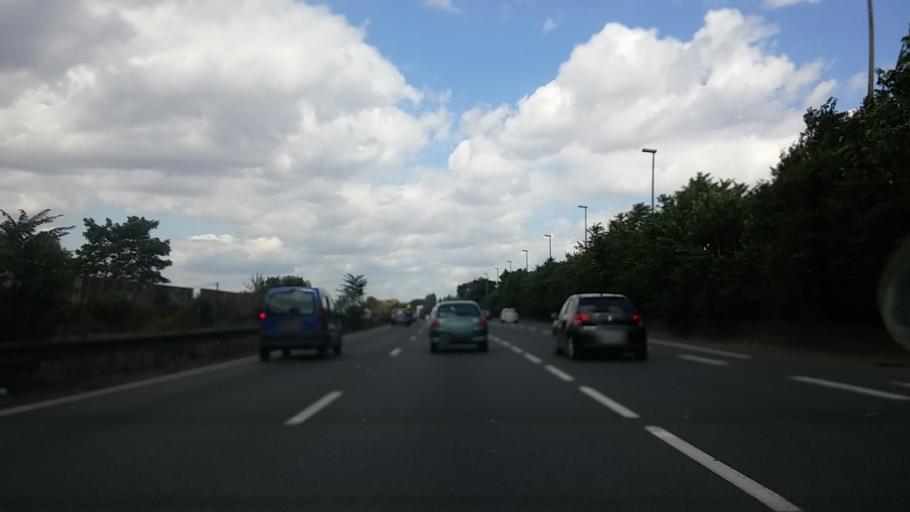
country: FR
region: Ile-de-France
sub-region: Departement de Seine-Saint-Denis
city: Aulnay-sous-Bois
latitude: 48.9238
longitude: 2.4809
